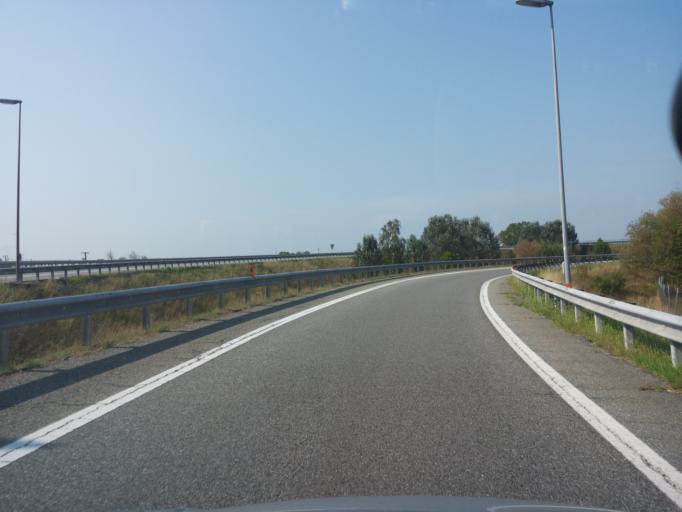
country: IT
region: Piedmont
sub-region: Provincia di Vercelli
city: Borgo Vercelli
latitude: 45.3649
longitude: 8.4881
